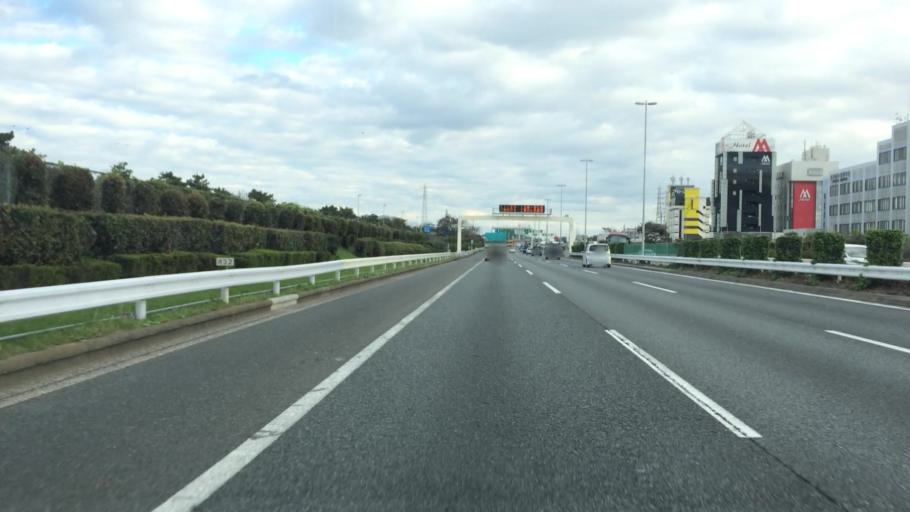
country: JP
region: Tokyo
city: Urayasu
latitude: 35.6669
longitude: 139.9215
